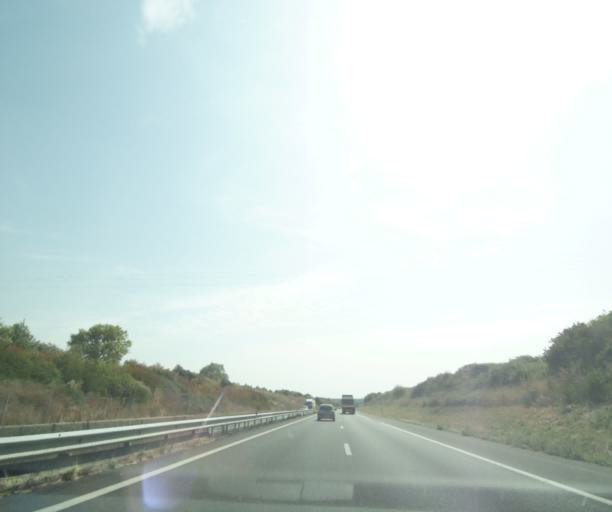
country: FR
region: Pays de la Loire
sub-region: Departement de la Vendee
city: Sainte-Hermine
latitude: 46.5515
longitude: -1.0921
